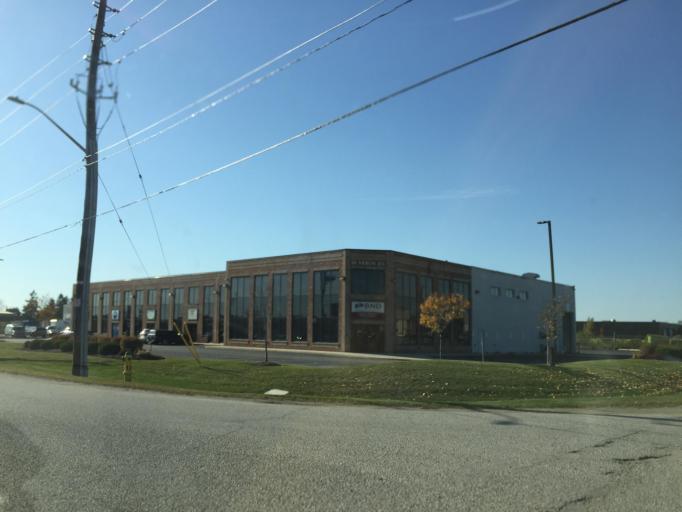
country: CA
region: Ontario
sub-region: Wellington County
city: Guelph
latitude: 43.5556
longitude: -80.2955
